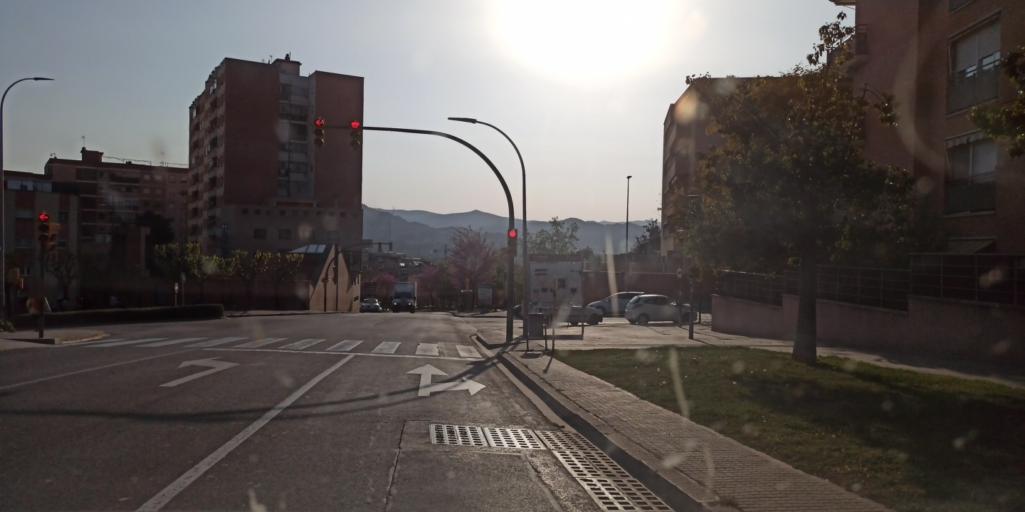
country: ES
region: Catalonia
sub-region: Provincia de Barcelona
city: Sant Feliu de Llobregat
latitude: 41.3892
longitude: 2.0468
